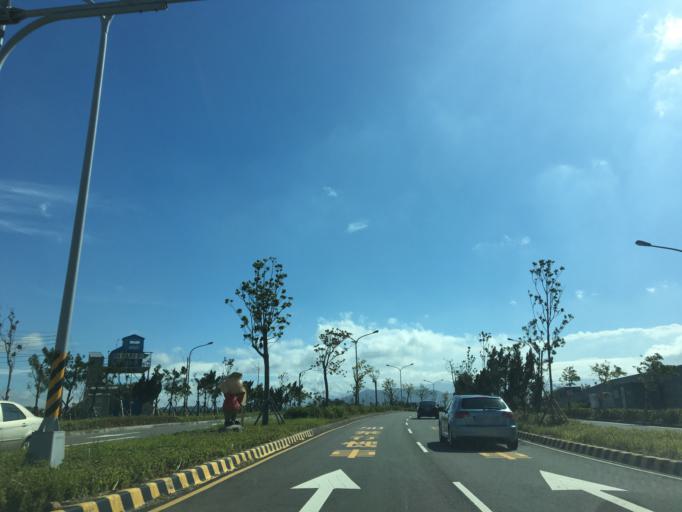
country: TW
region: Taiwan
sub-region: Hsinchu
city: Zhubei
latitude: 24.7817
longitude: 121.0496
